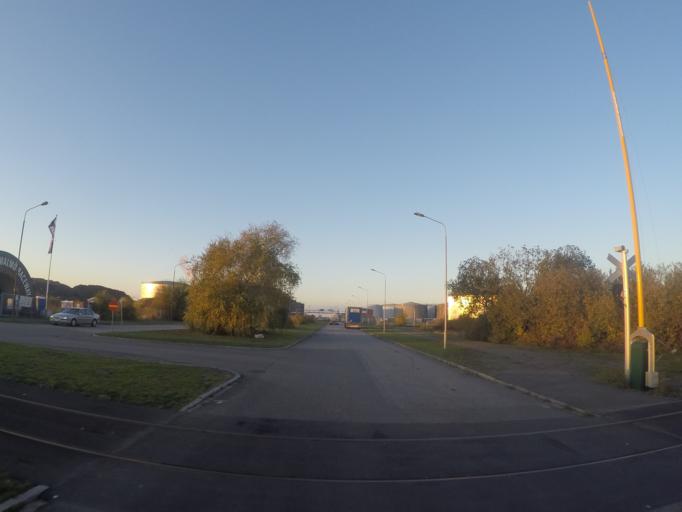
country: SE
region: Skane
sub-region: Burlovs Kommun
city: Arloev
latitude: 55.6308
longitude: 13.0363
